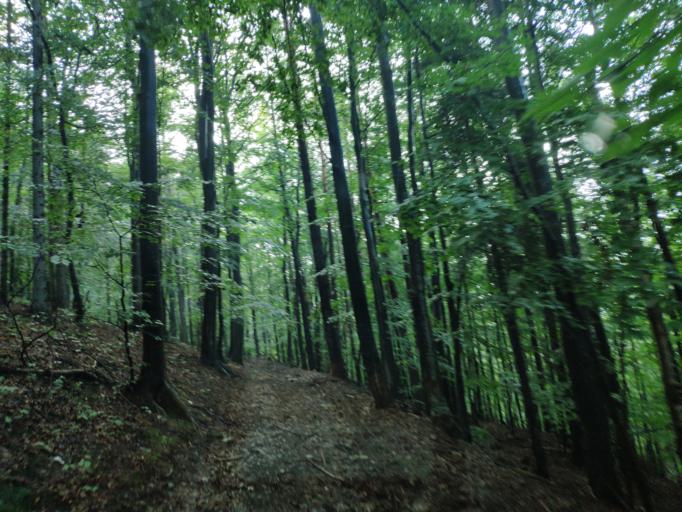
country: SK
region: Kosicky
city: Medzev
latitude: 48.7485
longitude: 20.9989
